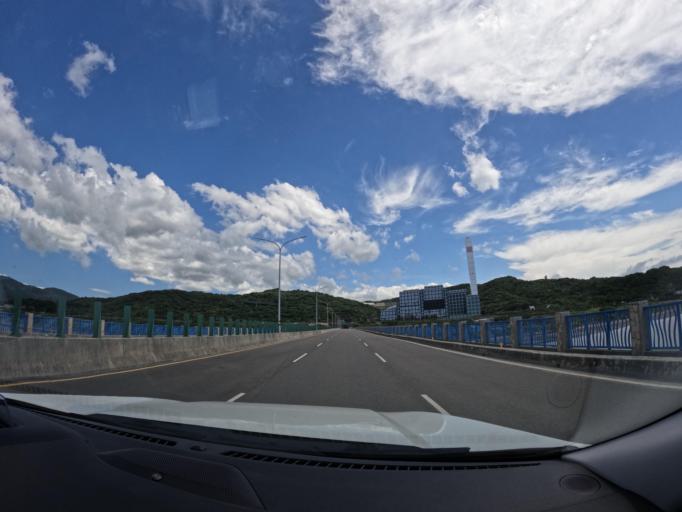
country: TW
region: Taiwan
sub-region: Taoyuan
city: Taoyuan
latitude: 25.1394
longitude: 121.3668
